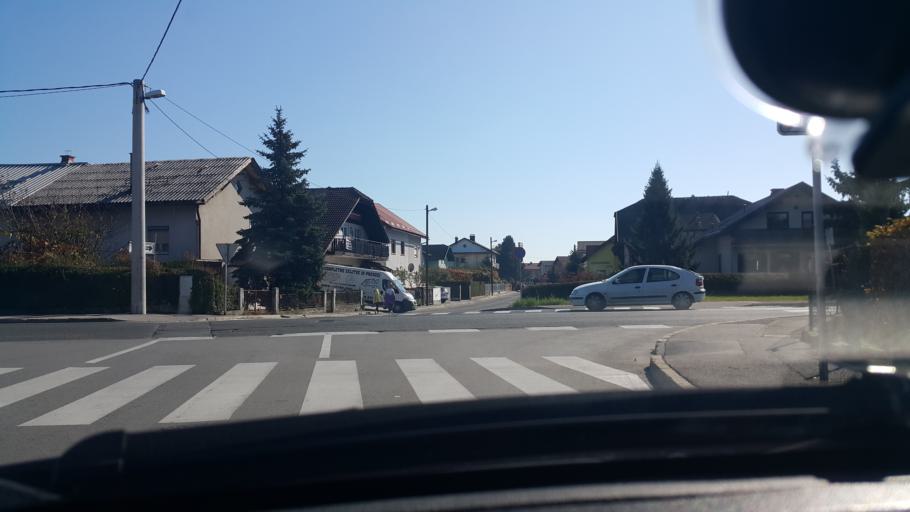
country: SI
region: Hoce-Slivnica
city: Rogoza
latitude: 46.5337
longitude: 15.6748
